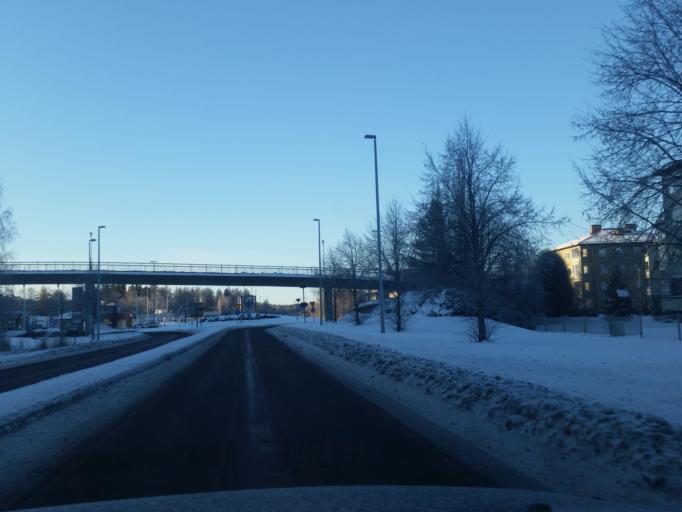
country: SE
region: Vaestmanland
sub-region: Arboga Kommun
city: Arboga
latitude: 59.3905
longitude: 15.8500
